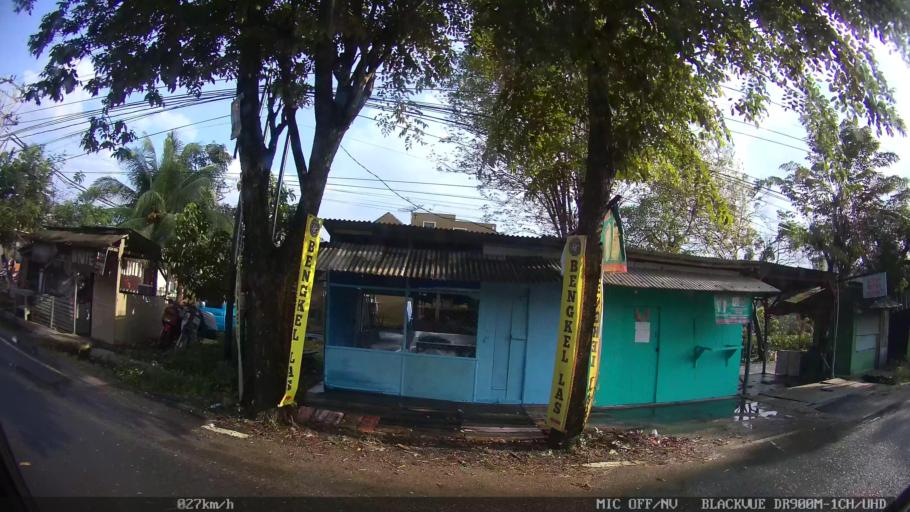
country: ID
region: Lampung
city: Kedaton
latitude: -5.3858
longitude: 105.3117
